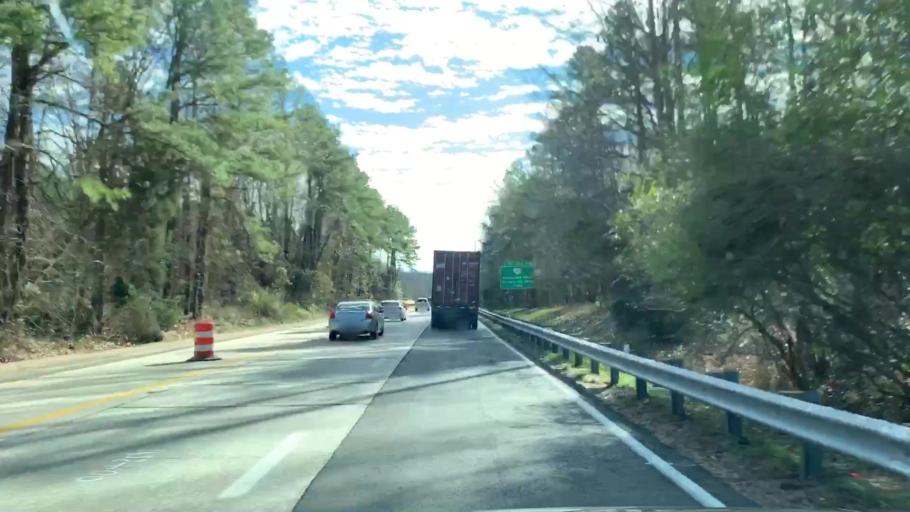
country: US
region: Virginia
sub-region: City of Williamsburg
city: Williamsburg
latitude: 37.2733
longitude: -76.6584
